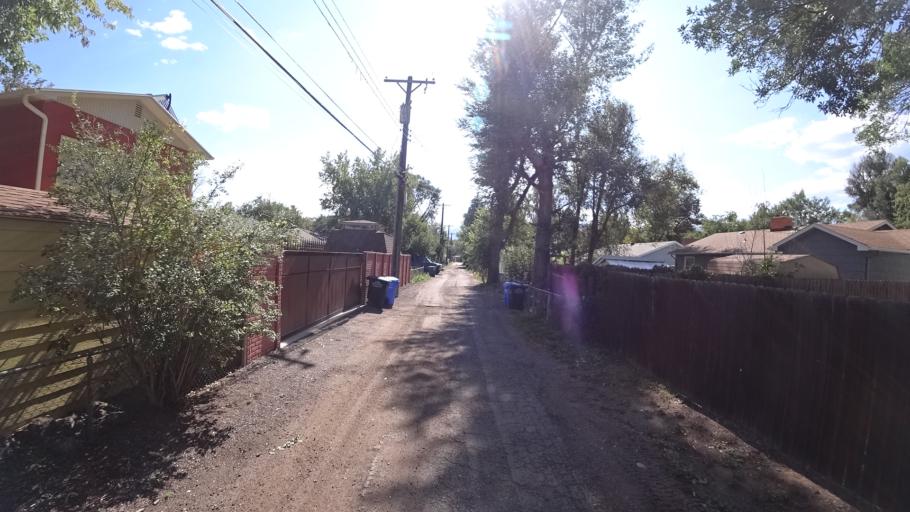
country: US
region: Colorado
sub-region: El Paso County
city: Colorado Springs
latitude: 38.8719
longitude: -104.8021
